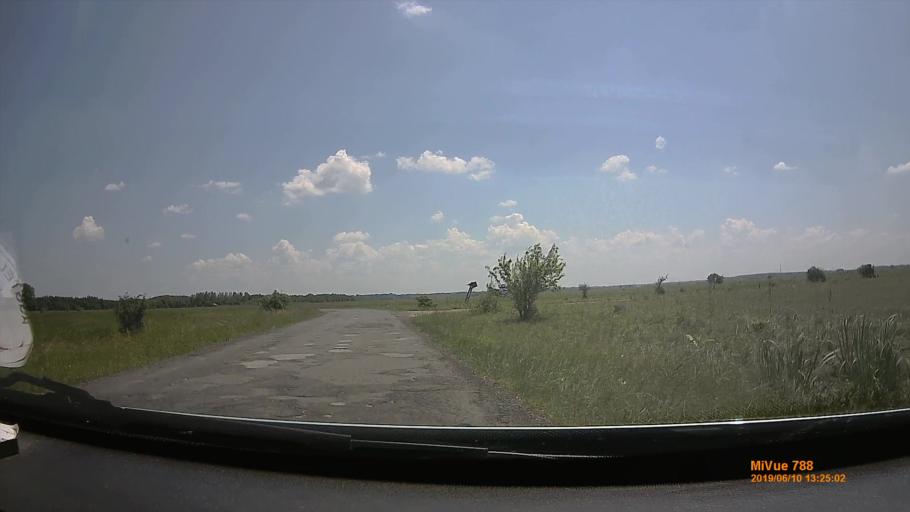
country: HU
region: Borsod-Abauj-Zemplen
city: Tiszaluc
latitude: 48.0175
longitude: 21.1059
